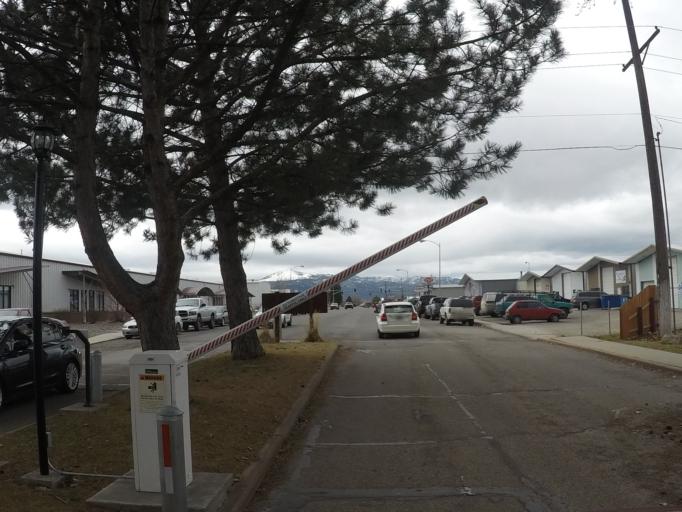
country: US
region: Montana
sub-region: Missoula County
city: Missoula
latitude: 46.8871
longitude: -114.0235
